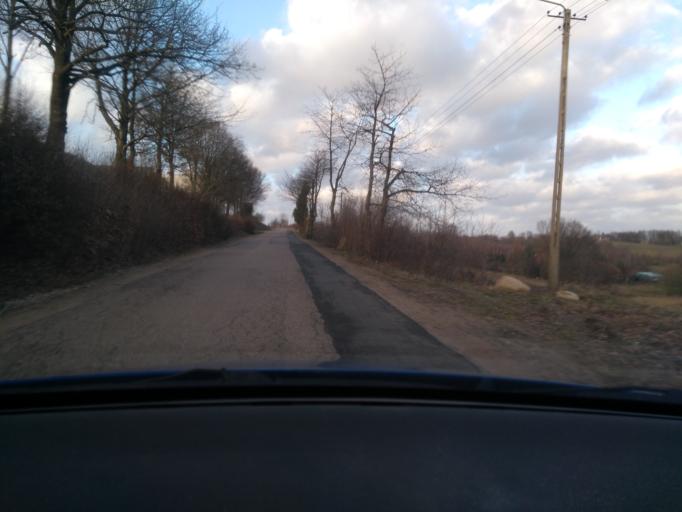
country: PL
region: Pomeranian Voivodeship
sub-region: Powiat kartuski
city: Kartuzy
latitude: 54.3817
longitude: 18.2192
